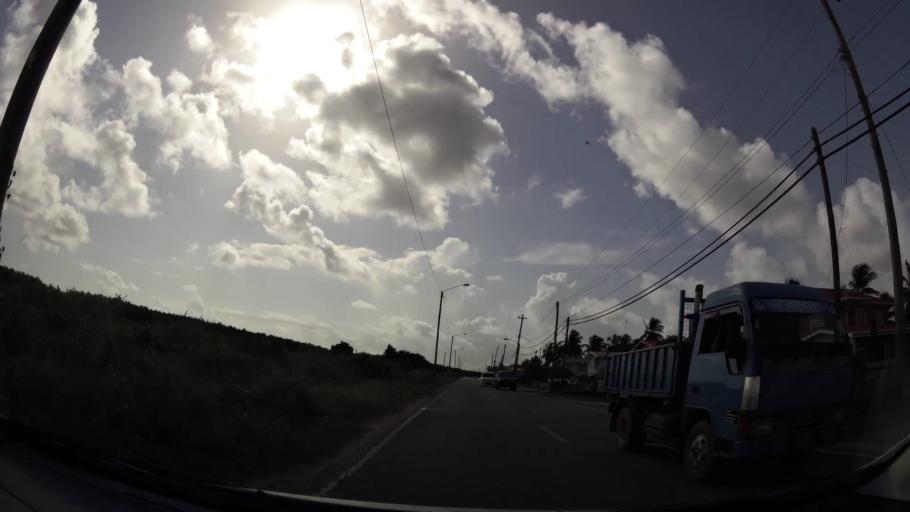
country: GY
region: Demerara-Mahaica
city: Mahaica Village
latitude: 6.7467
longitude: -57.9599
